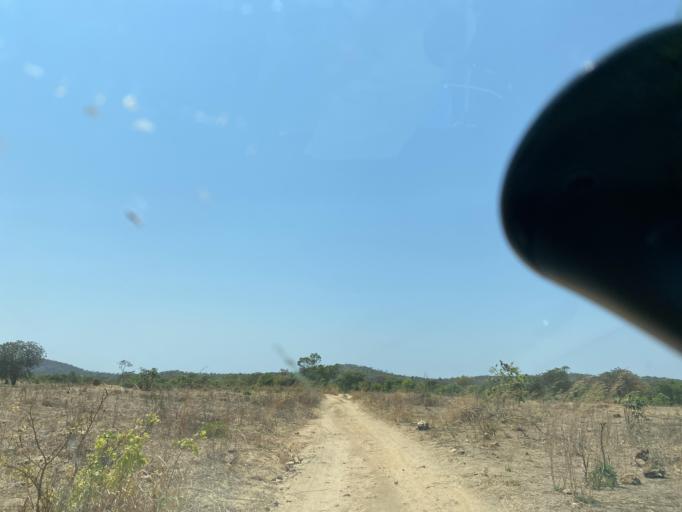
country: ZM
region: Lusaka
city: Chongwe
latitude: -15.4329
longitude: 29.1931
